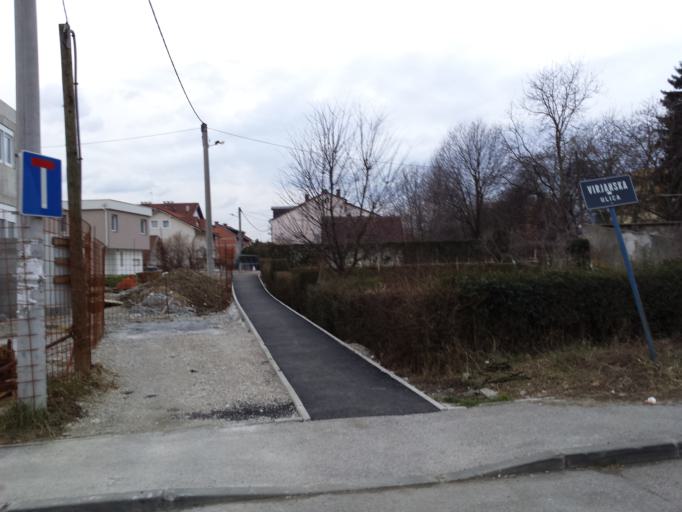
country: HR
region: Grad Zagreb
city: Jankomir
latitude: 45.7996
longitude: 15.9266
